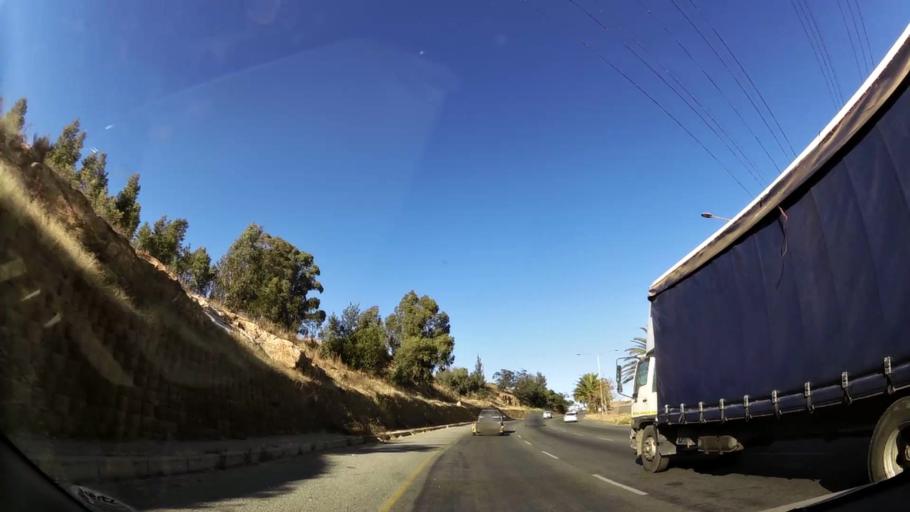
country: ZA
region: Gauteng
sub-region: West Rand District Municipality
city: Krugersdorp
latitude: -26.1100
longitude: 27.7777
